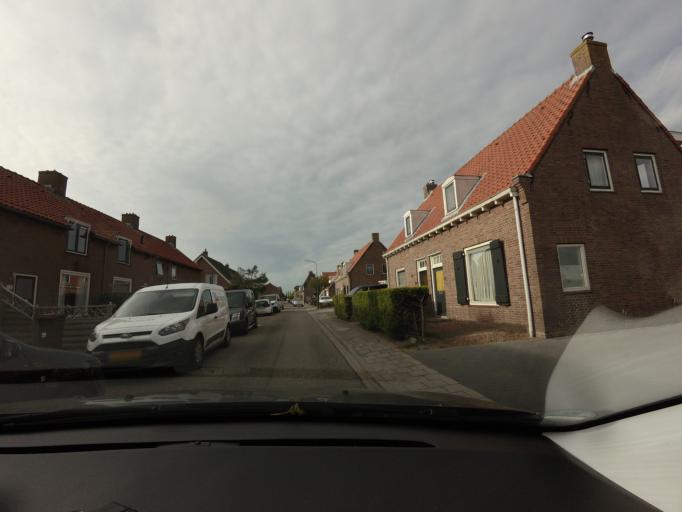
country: NL
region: Utrecht
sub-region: Gemeente IJsselstein
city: IJsselstein
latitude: 51.9820
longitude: 5.0153
